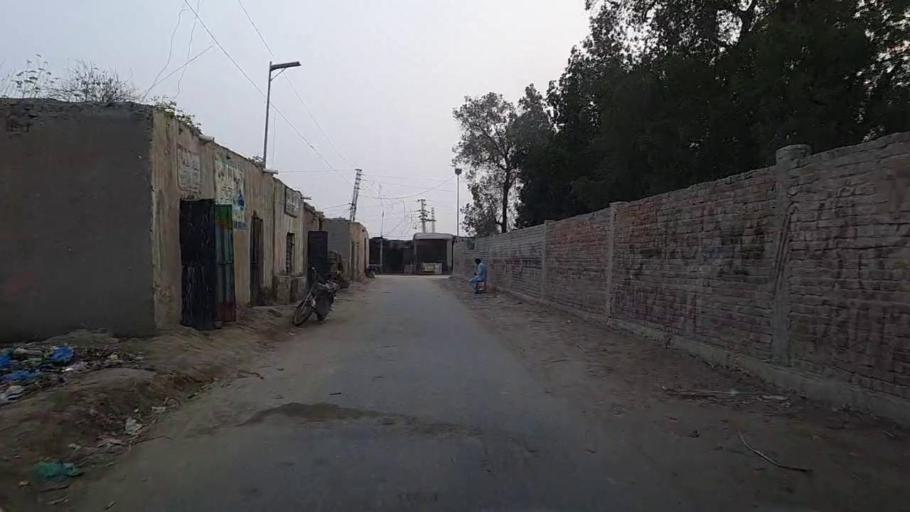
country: PK
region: Sindh
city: Kandiari
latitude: 26.9262
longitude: 68.5008
